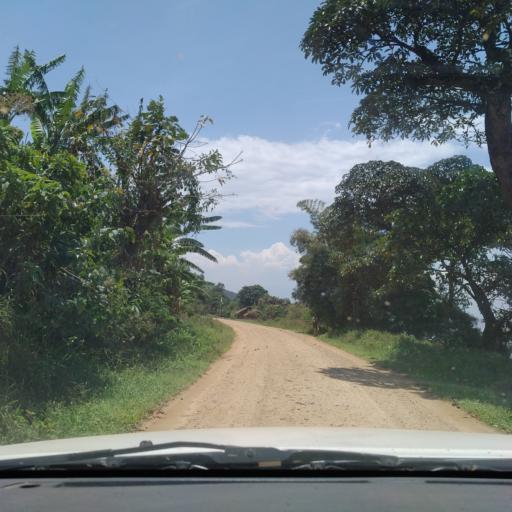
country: CD
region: Nord Kivu
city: Sake
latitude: -1.9078
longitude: 28.9821
